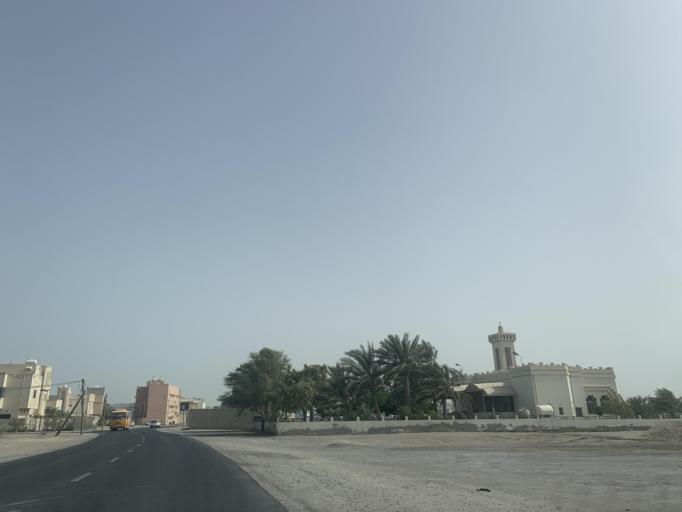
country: BH
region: Northern
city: Sitrah
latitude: 26.1736
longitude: 50.6201
